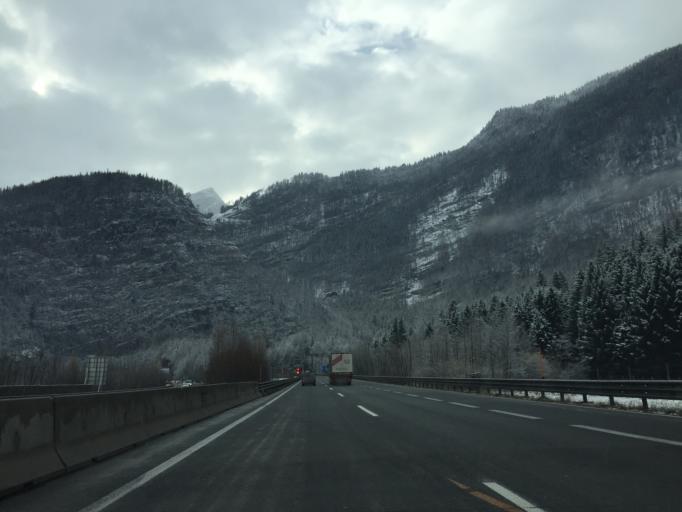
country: AT
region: Salzburg
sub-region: Politischer Bezirk Hallein
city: Golling an der Salzach
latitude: 47.5817
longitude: 13.1584
